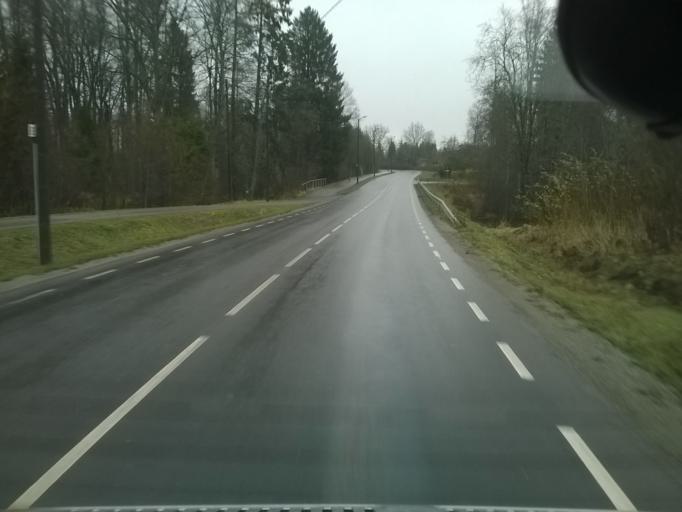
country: EE
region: Harju
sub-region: Saku vald
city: Saku
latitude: 59.2279
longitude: 24.6763
